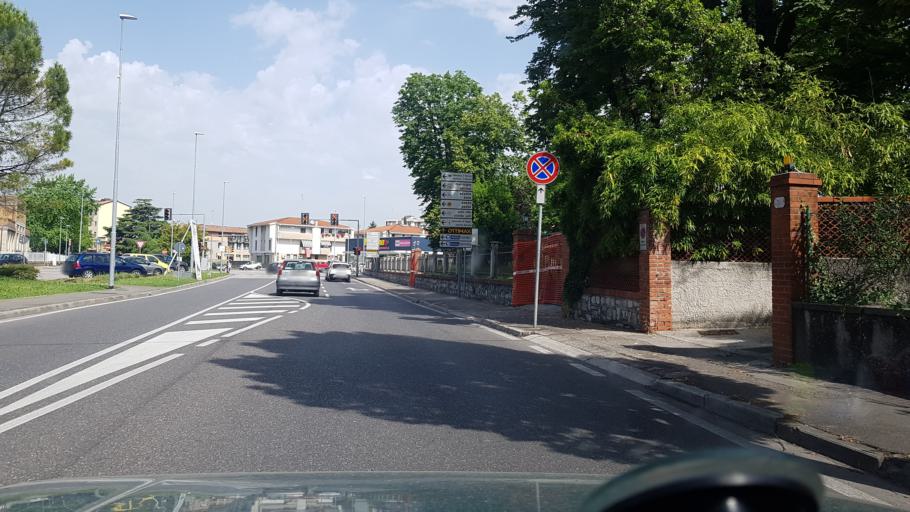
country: IT
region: Friuli Venezia Giulia
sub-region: Provincia di Gorizia
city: Ronchi dei Legionari
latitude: 45.8263
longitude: 13.5056
